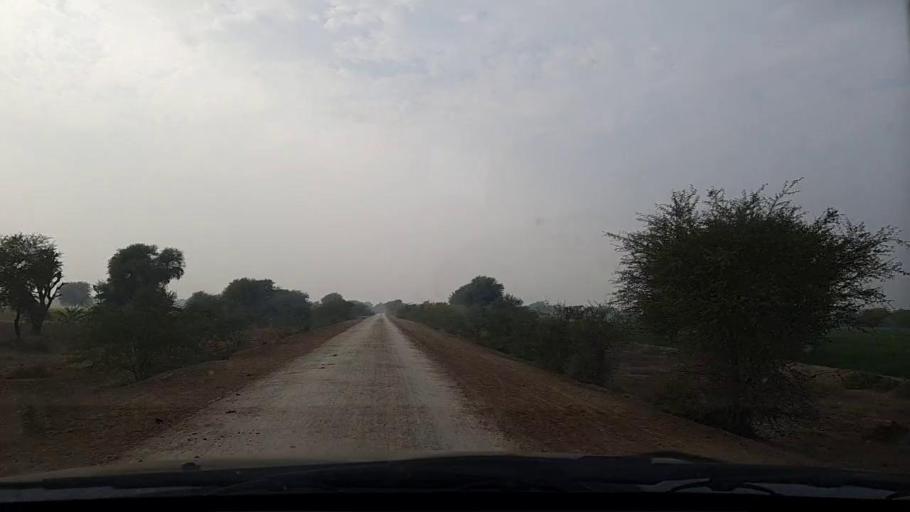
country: PK
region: Sindh
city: Pithoro
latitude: 25.7100
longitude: 69.3939
